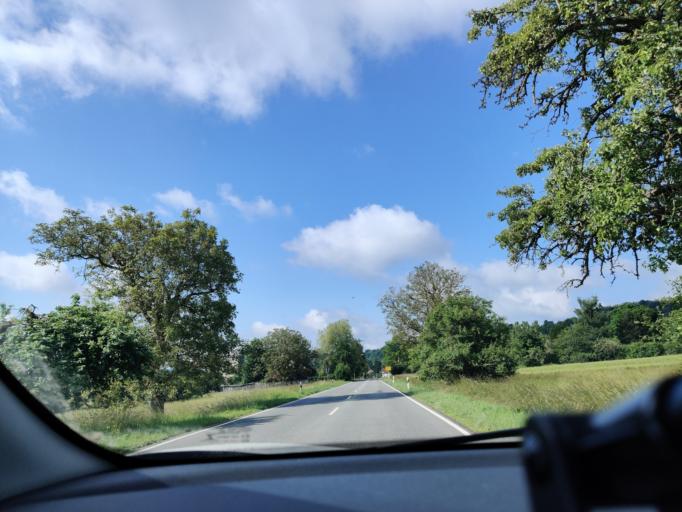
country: DE
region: Saarland
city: Gersheim
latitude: 49.1896
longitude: 7.1643
